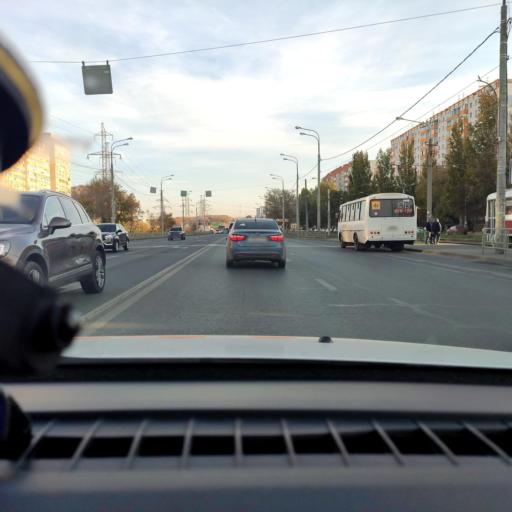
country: RU
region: Samara
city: Samara
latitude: 53.2647
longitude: 50.2186
